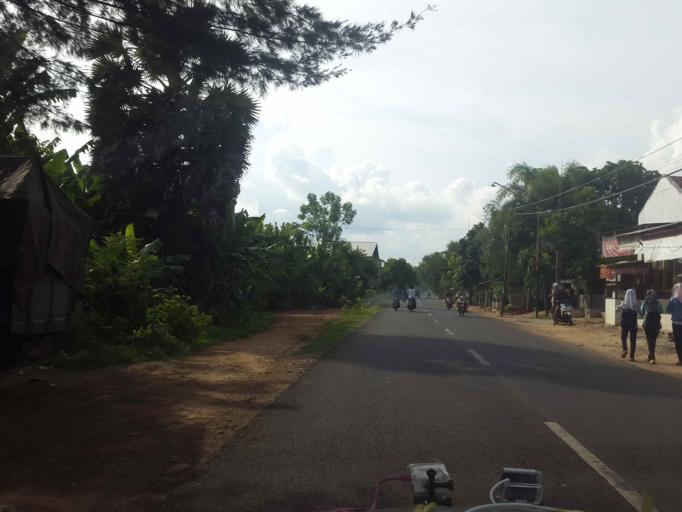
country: ID
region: East Java
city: Bereklorong
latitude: -7.0382
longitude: 113.9121
